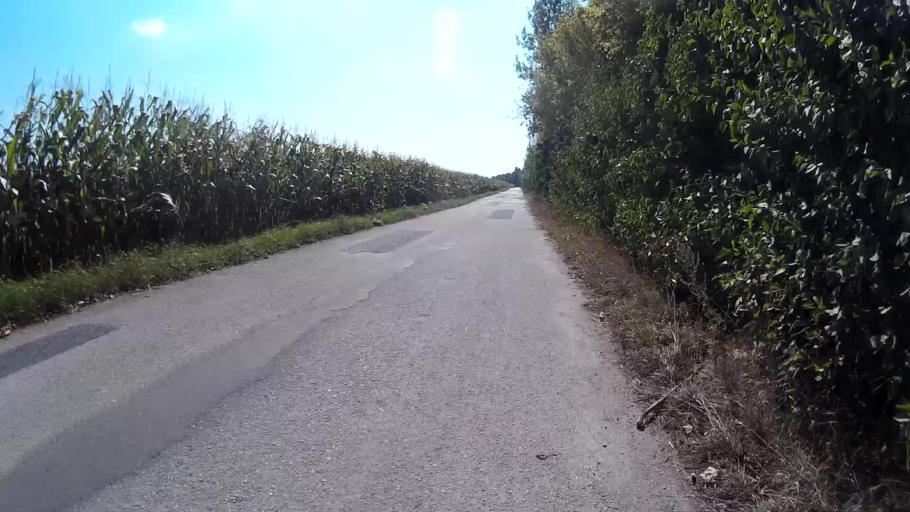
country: AT
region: Lower Austria
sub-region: Politischer Bezirk Mistelbach
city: Neudorf bei Staatz
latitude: 48.7656
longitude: 16.4885
